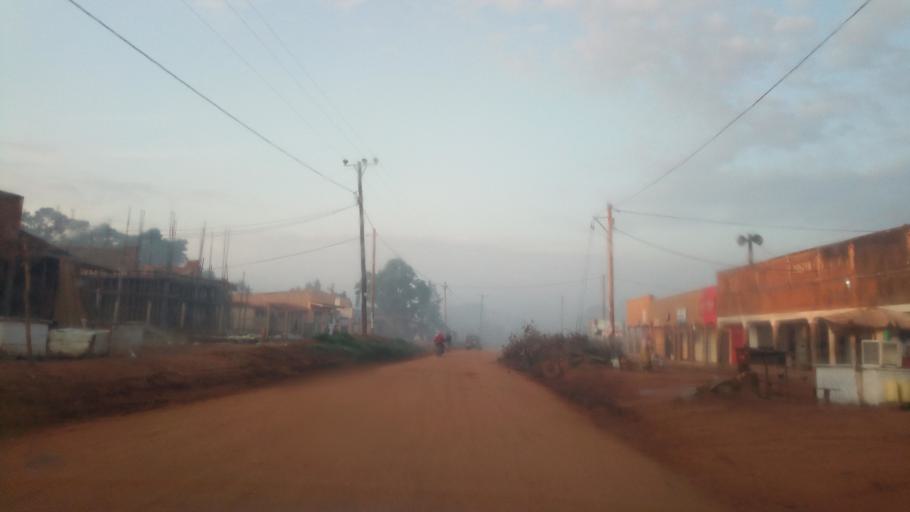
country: UG
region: Central Region
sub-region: Wakiso District
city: Bweyogerere
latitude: 0.4388
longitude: 32.6552
